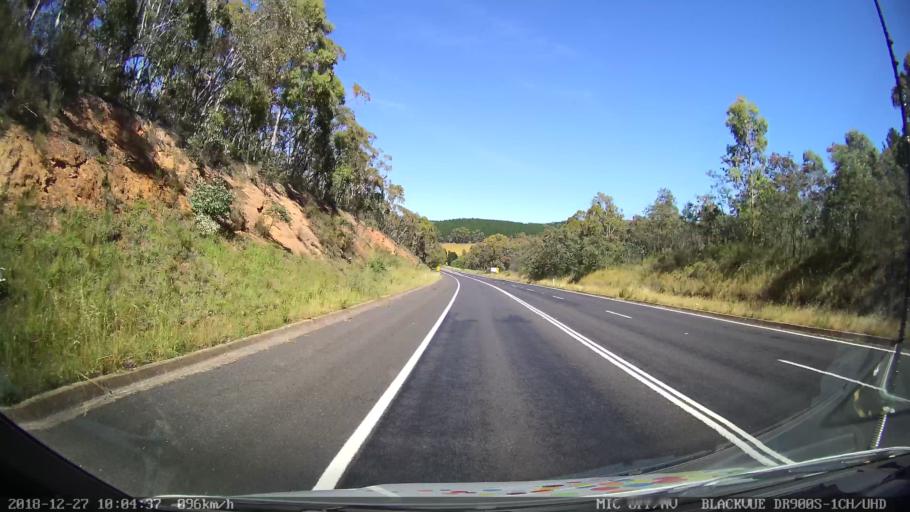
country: AU
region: New South Wales
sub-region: Lithgow
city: Portland
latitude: -33.4325
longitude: 149.8853
